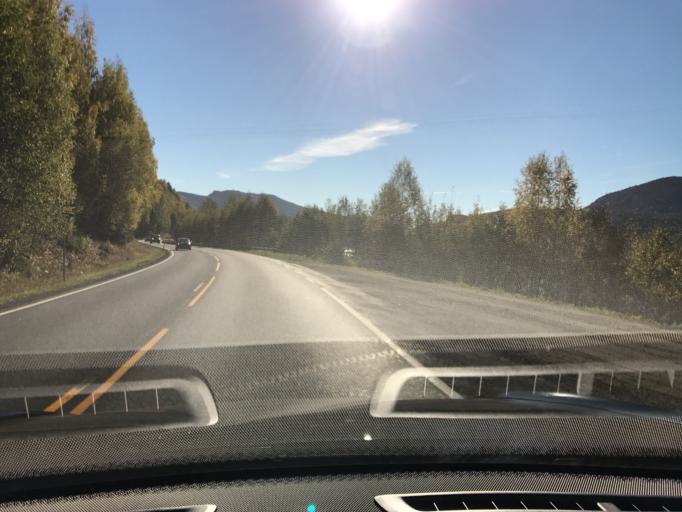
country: NO
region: Buskerud
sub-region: Krodsherad
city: Noresund
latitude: 60.3133
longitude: 9.6746
